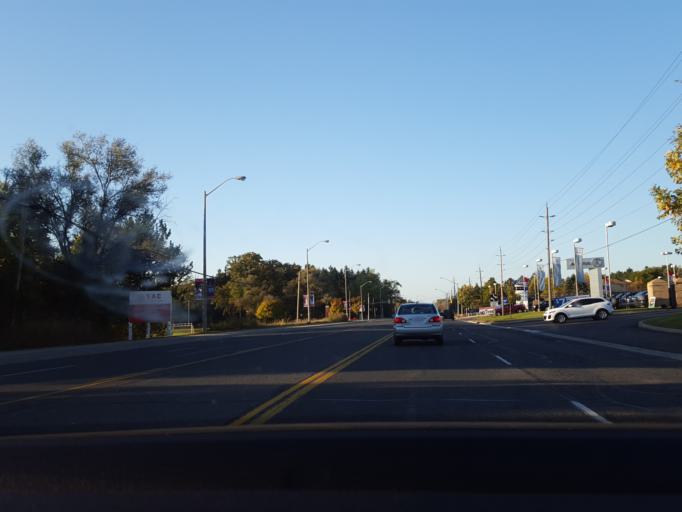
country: CA
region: Ontario
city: Newmarket
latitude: 44.0121
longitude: -79.4705
